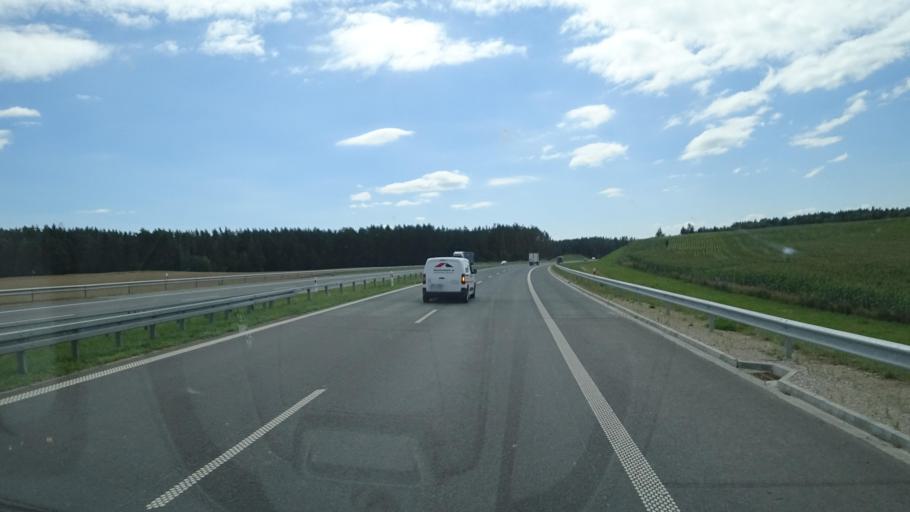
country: PL
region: Podlasie
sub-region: Powiat grajewski
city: Szczuczyn
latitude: 53.5236
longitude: 22.2601
